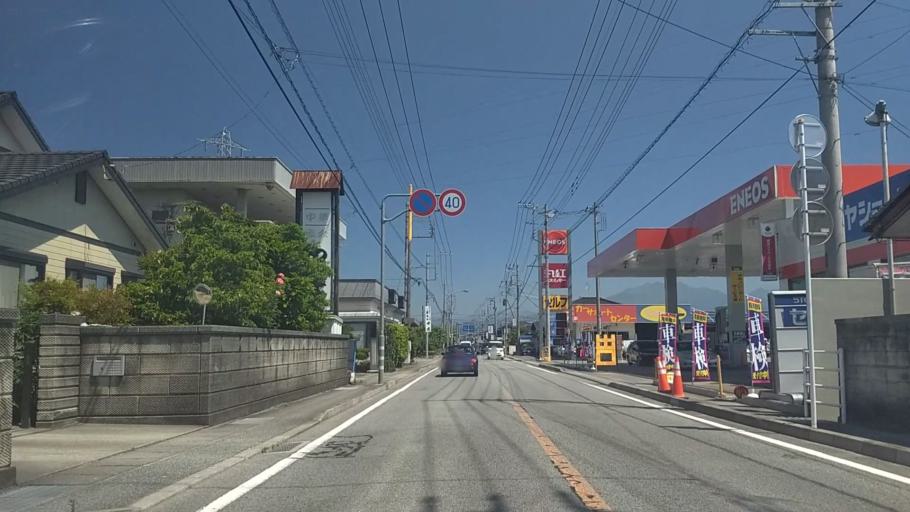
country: JP
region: Yamanashi
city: Ryuo
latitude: 35.6597
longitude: 138.4650
